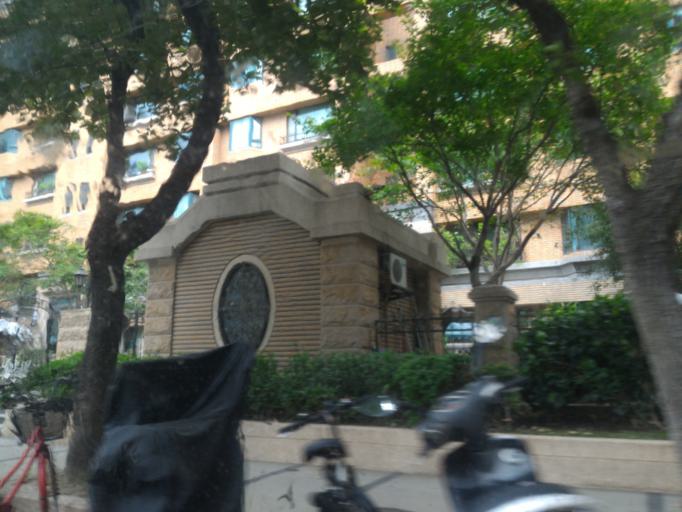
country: TW
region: Taipei
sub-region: Taipei
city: Banqiao
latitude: 25.0876
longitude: 121.4587
